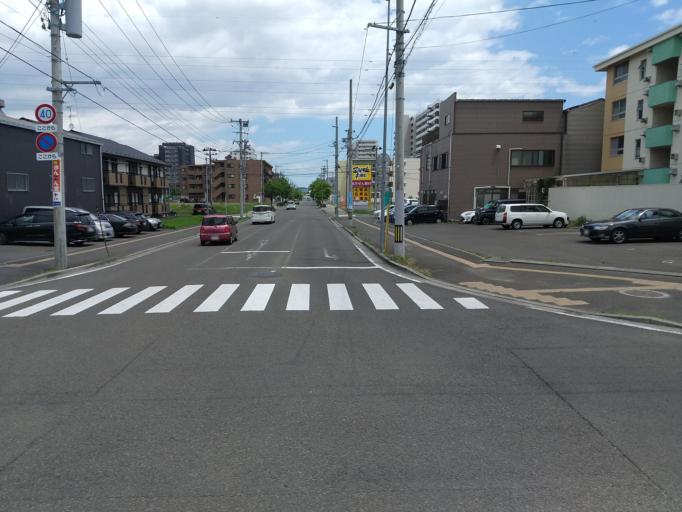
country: JP
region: Miyagi
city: Sendai-shi
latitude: 38.2768
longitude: 140.9302
